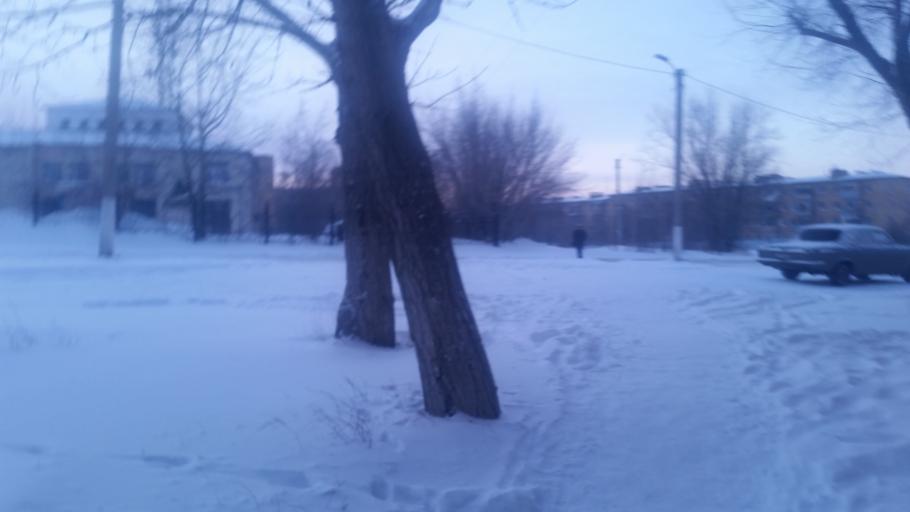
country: KZ
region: Qaraghandy
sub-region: Qaraghandy Qalasy
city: Karagandy
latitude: 49.8996
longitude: 73.0772
